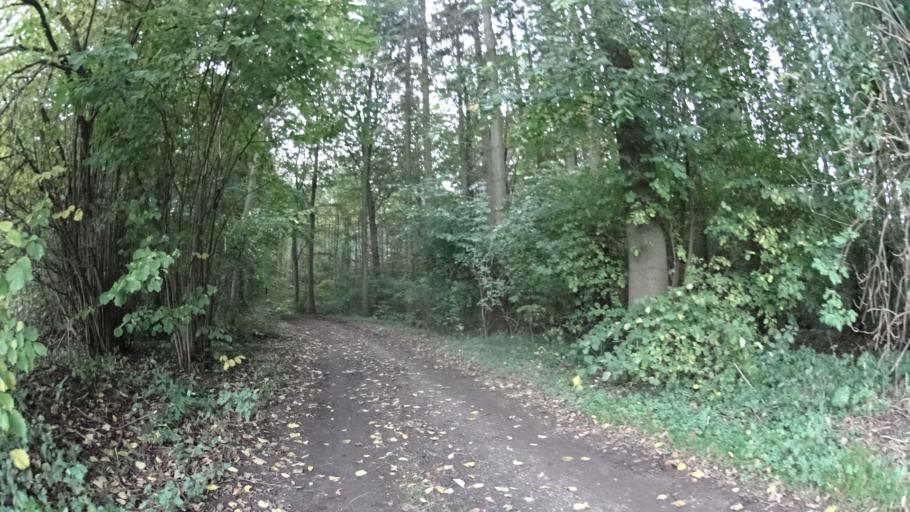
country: DK
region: Central Jutland
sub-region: Arhus Kommune
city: Kolt
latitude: 56.1384
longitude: 10.0850
